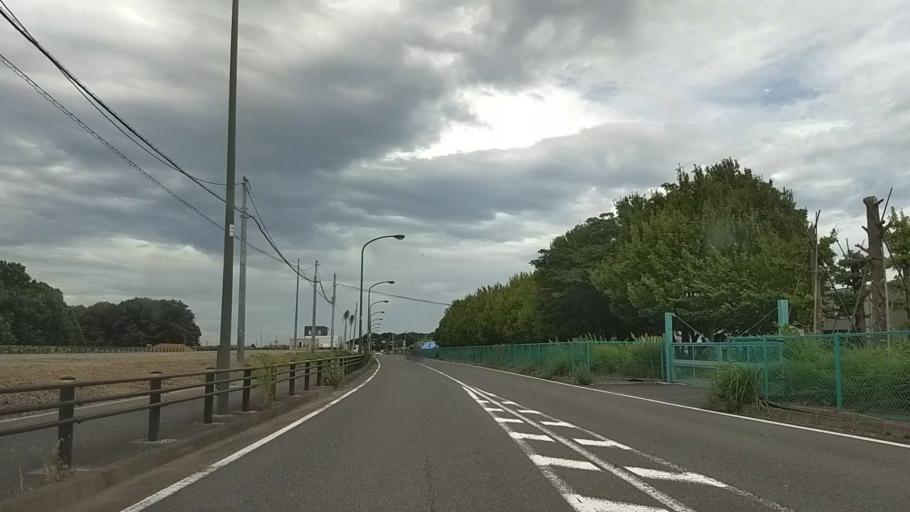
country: JP
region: Tokyo
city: Hachioji
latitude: 35.6357
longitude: 139.3262
